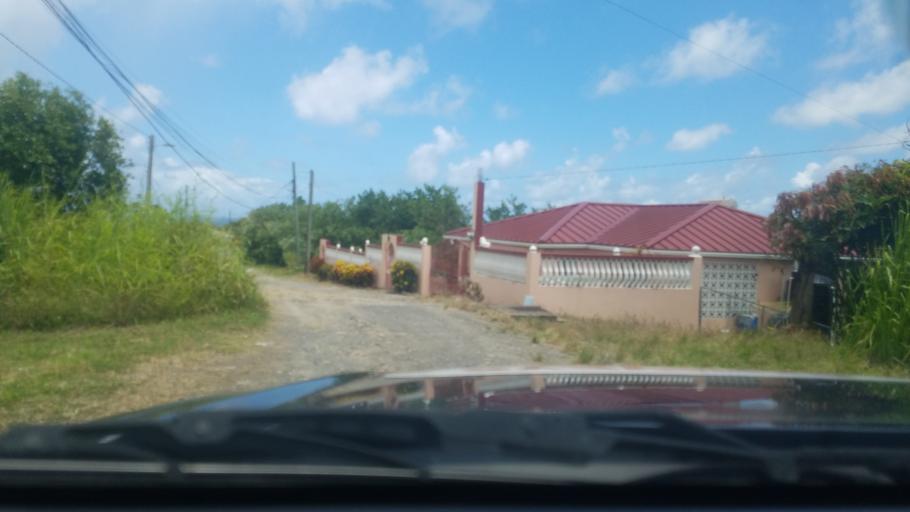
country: LC
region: Dennery Quarter
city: Dennery
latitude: 13.9185
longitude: -60.8951
